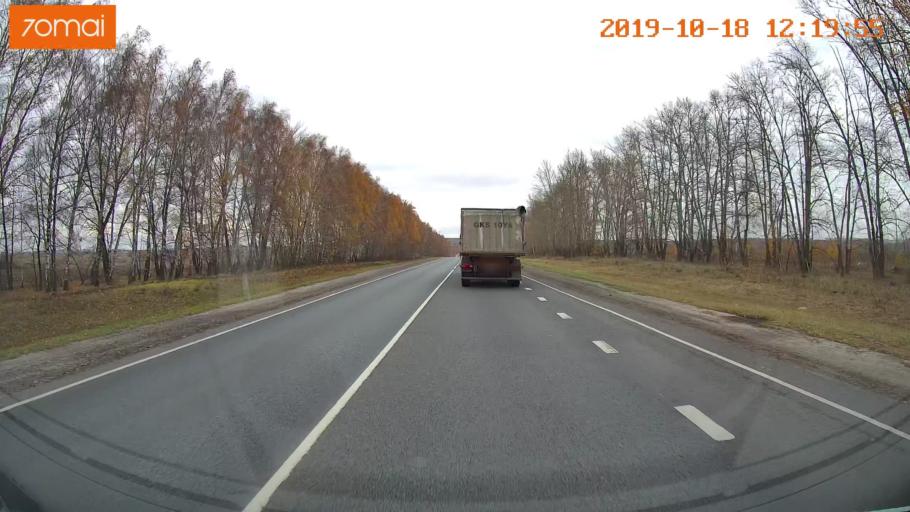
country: RU
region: Rjazan
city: Zakharovo
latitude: 54.4895
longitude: 39.4738
